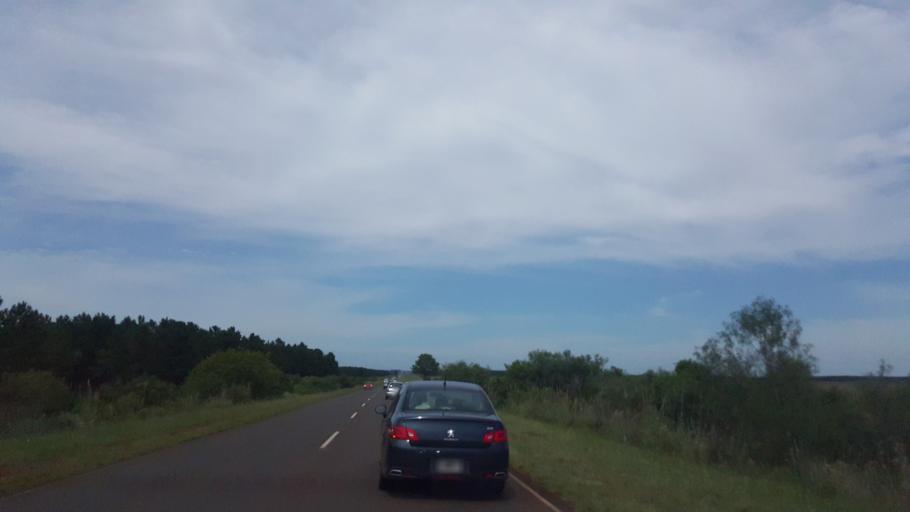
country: PY
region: Itapua
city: San Juan del Parana
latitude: -27.5077
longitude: -56.1293
